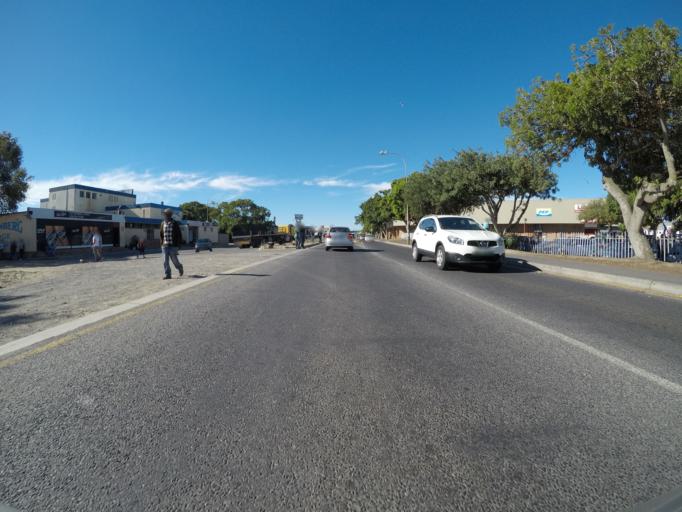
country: ZA
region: Western Cape
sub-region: City of Cape Town
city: Kraaifontein
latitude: -33.9258
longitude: 18.6767
